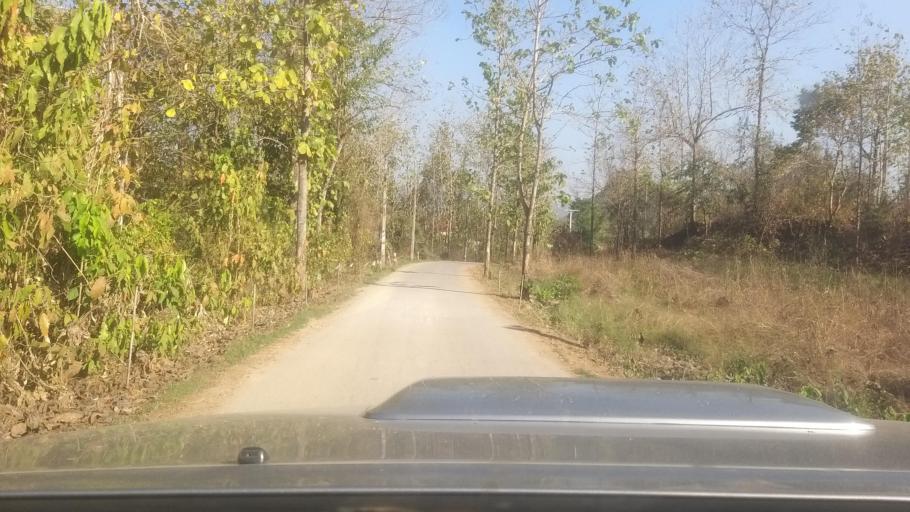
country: TH
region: Phrae
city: Phrae
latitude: 18.2646
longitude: 99.9851
